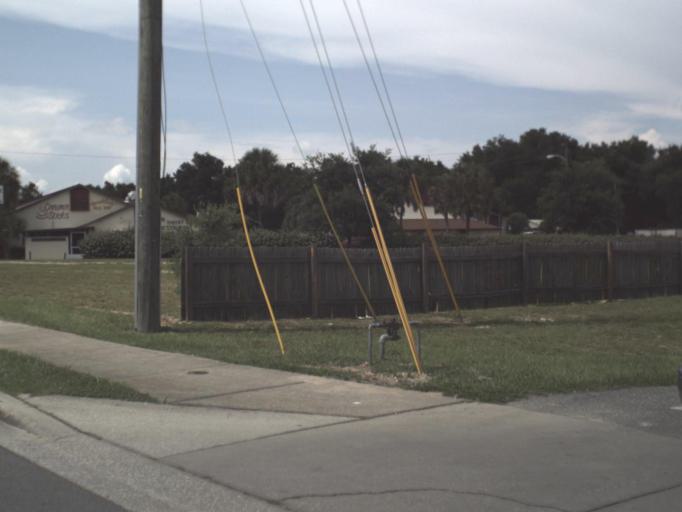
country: US
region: Florida
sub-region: Citrus County
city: Inverness
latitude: 28.8237
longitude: -82.3184
